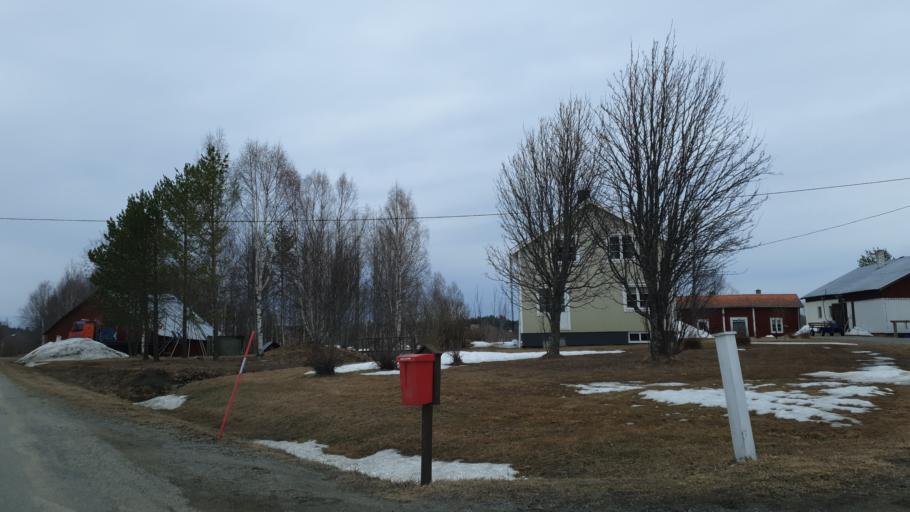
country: SE
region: Vaesterbotten
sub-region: Robertsfors Kommun
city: Robertsfors
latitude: 64.3945
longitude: 21.0016
